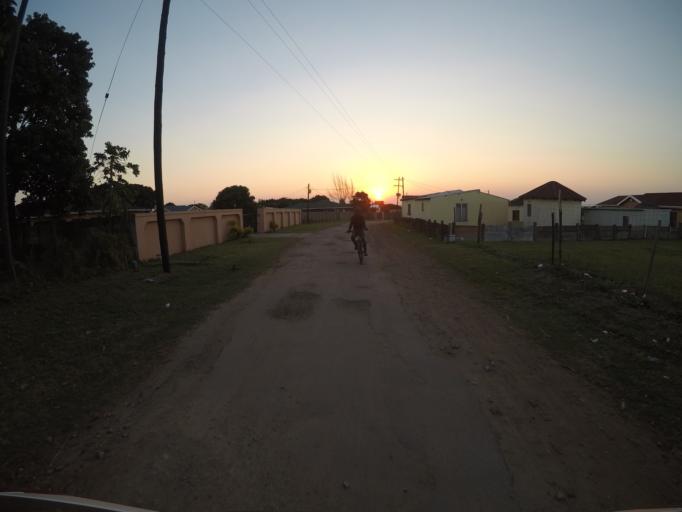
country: ZA
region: KwaZulu-Natal
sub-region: uThungulu District Municipality
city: Richards Bay
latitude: -28.7595
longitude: 32.1278
